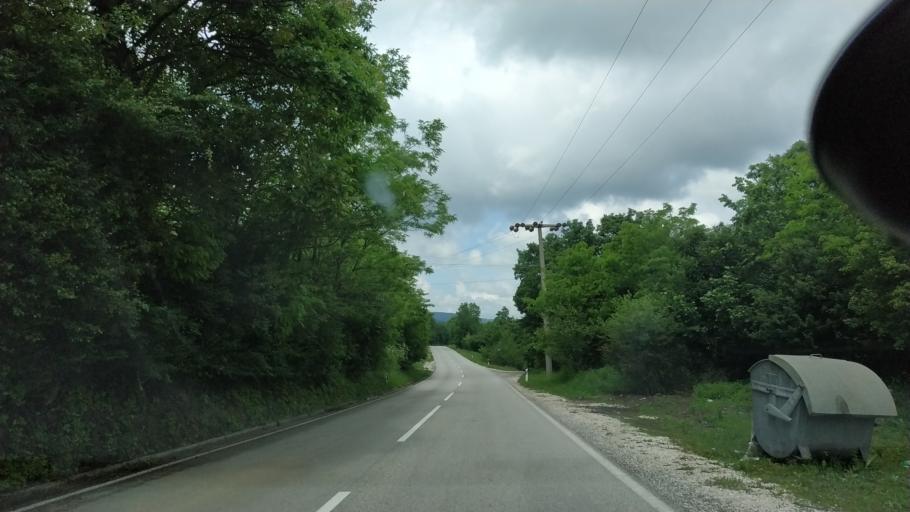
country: RS
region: Central Serbia
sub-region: Borski Okrug
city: Bor
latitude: 44.0741
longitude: 22.0265
